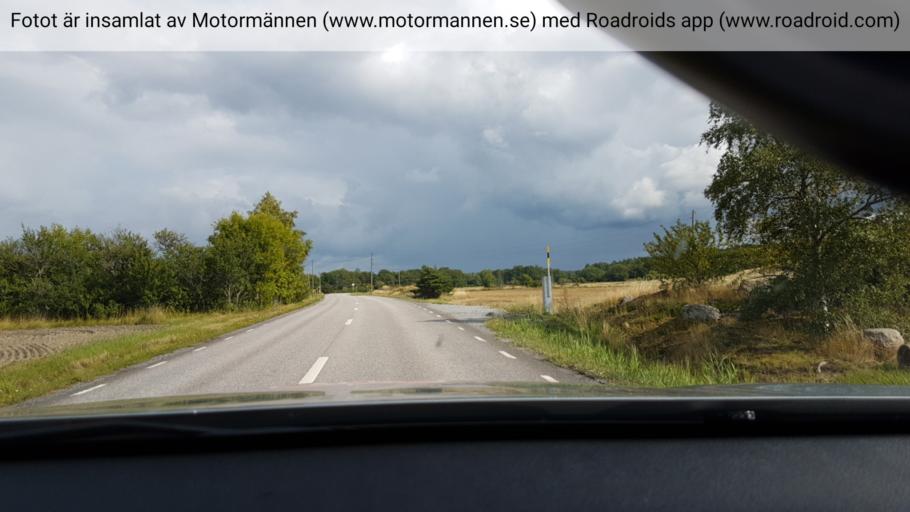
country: SE
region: Stockholm
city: Stenhamra
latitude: 59.3898
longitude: 17.6718
